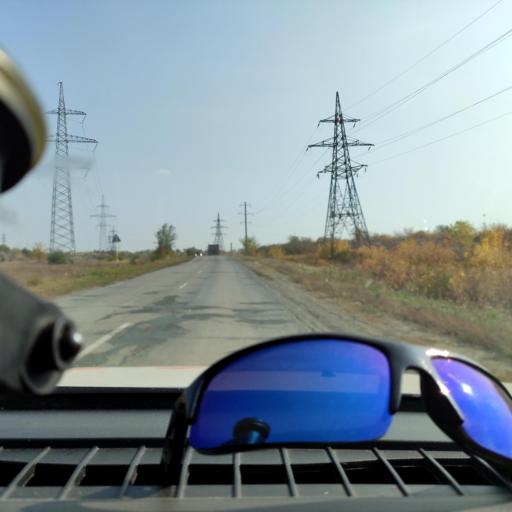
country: RU
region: Samara
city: Chapayevsk
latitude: 53.0018
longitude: 49.7561
